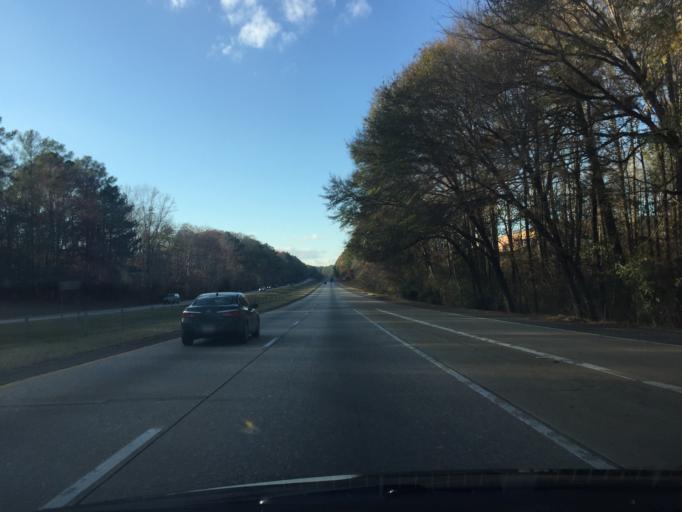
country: US
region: Georgia
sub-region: Bibb County
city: Macon
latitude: 32.9306
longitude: -83.7358
